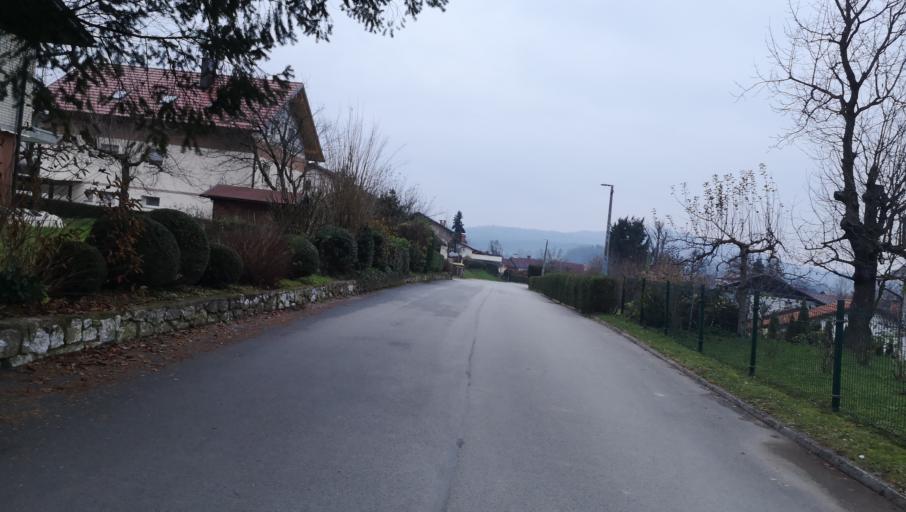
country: SI
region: Novo Mesto
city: Novo Mesto
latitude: 45.8196
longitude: 15.1612
